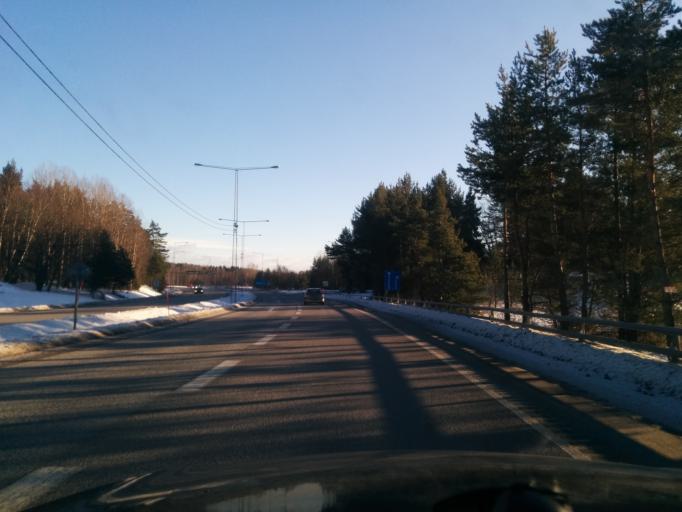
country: SE
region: Stockholm
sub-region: Taby Kommun
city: Taby
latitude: 59.4577
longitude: 18.1325
